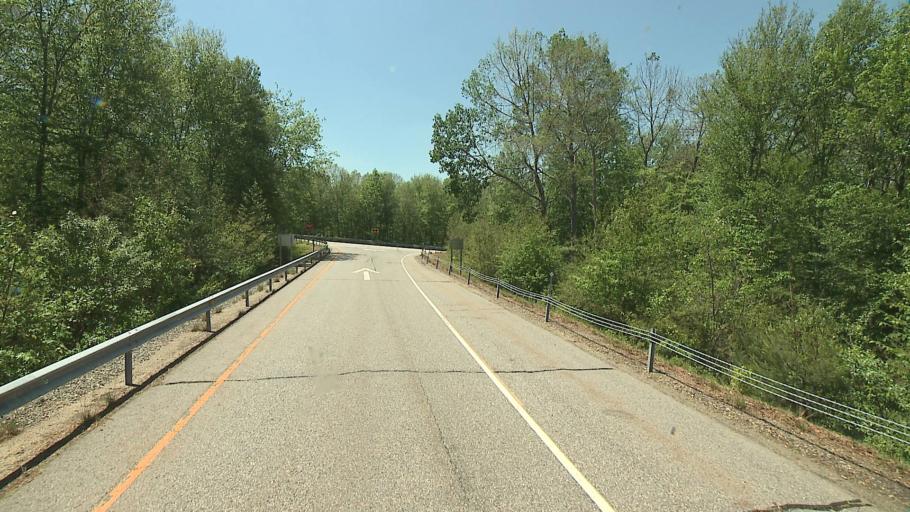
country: US
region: Connecticut
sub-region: Windham County
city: Danielson
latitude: 41.7678
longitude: -71.8688
